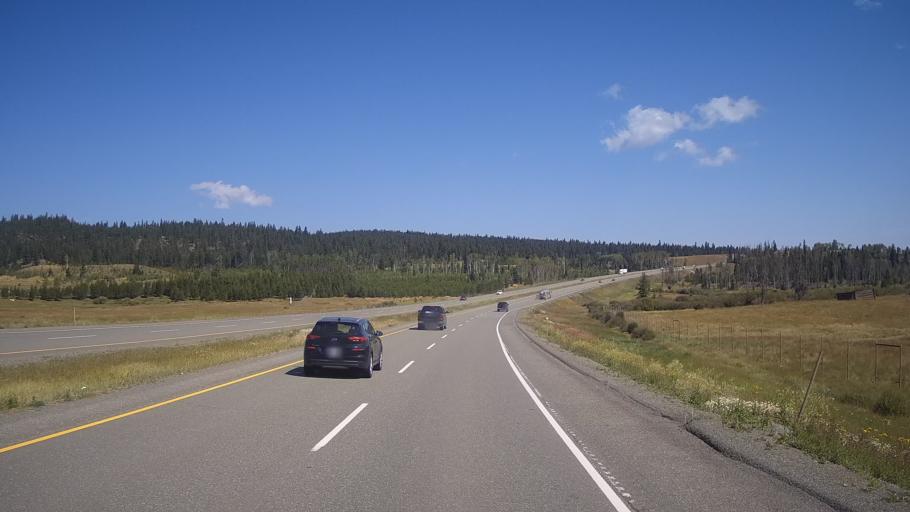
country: CA
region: British Columbia
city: Logan Lake
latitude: 50.4587
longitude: -120.5913
